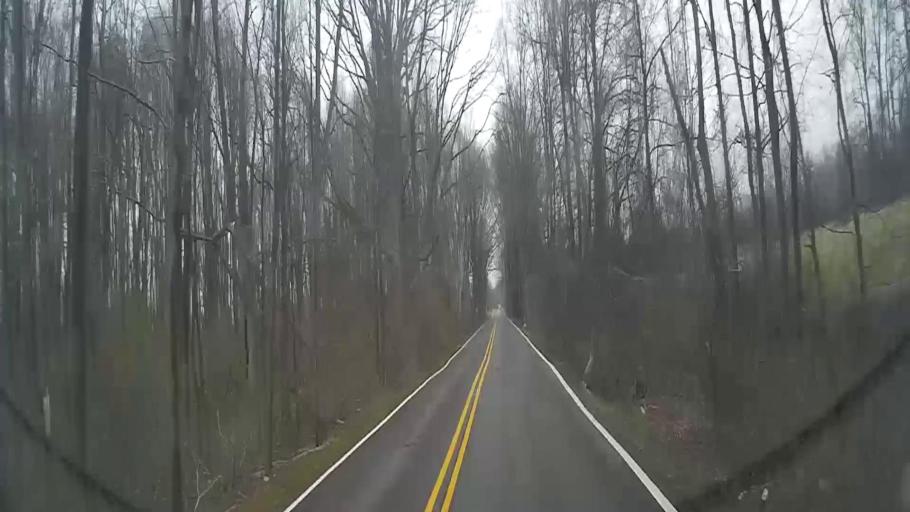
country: US
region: New Jersey
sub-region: Burlington County
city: Marlton
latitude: 39.8781
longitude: -74.8857
